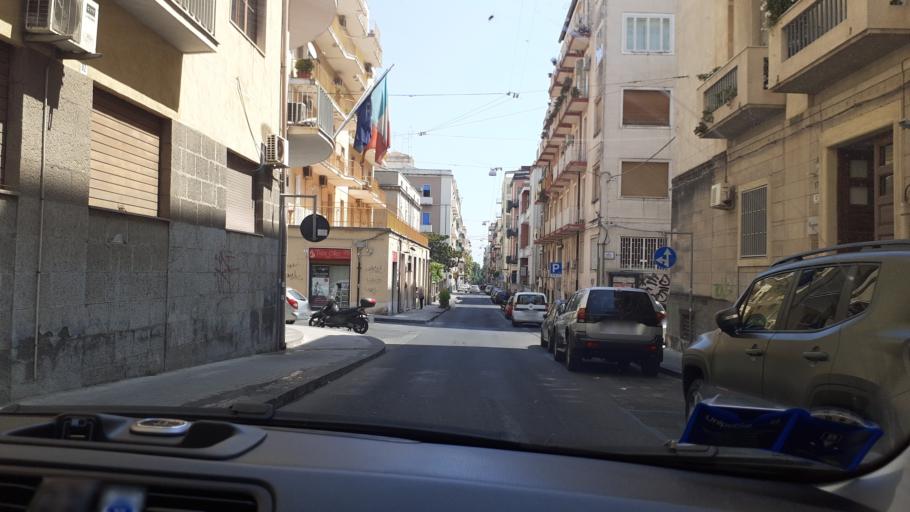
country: IT
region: Sicily
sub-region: Catania
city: Catania
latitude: 37.5095
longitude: 15.0760
